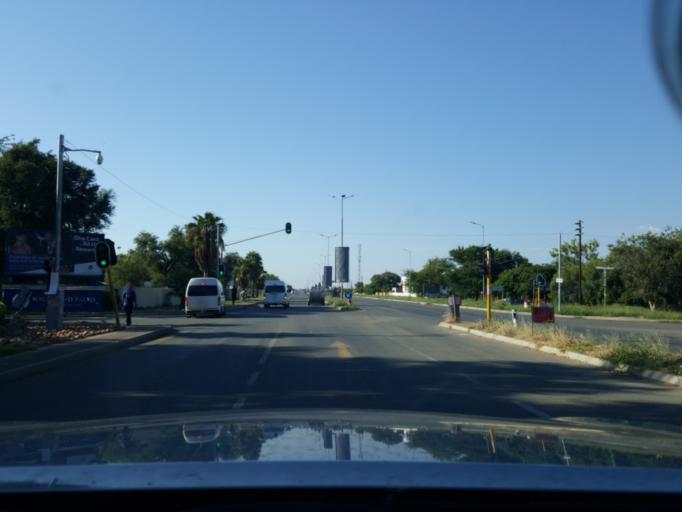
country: ZA
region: North-West
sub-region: Ngaka Modiri Molema District Municipality
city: Mmabatho
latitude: -25.8168
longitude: 25.6340
